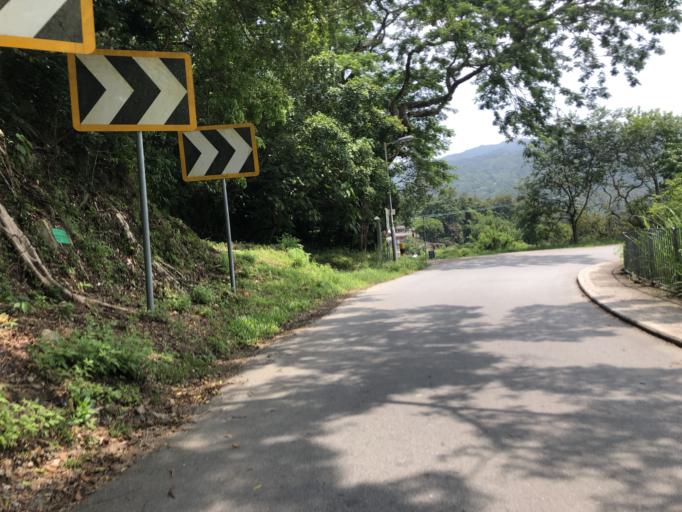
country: CN
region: Guangdong
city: Haishan
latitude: 22.5246
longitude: 114.2105
